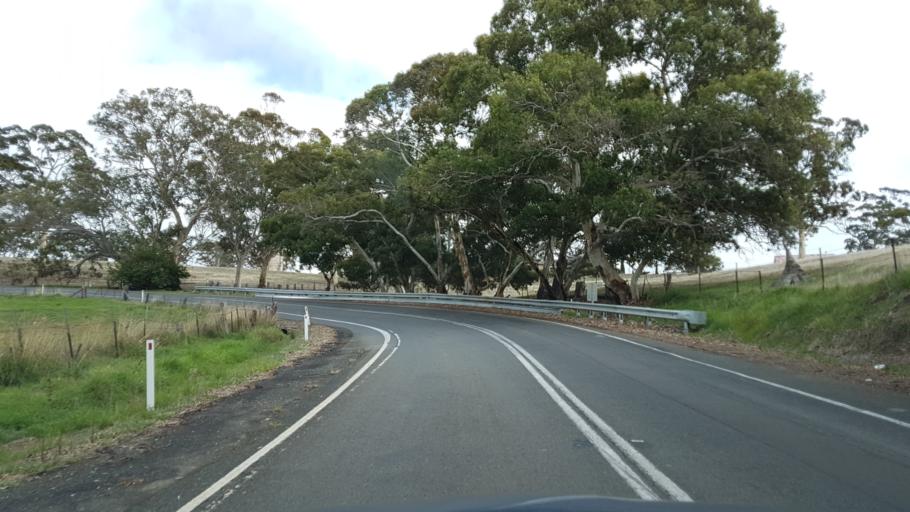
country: AU
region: South Australia
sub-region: Mount Barker
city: Nairne
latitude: -35.0405
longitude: 138.9403
